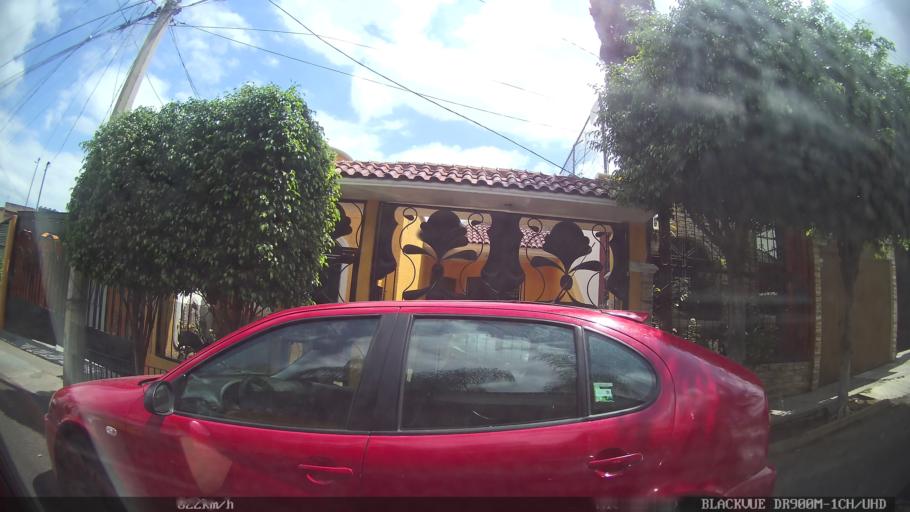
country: MX
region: Jalisco
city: Tonala
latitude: 20.6292
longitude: -103.2536
